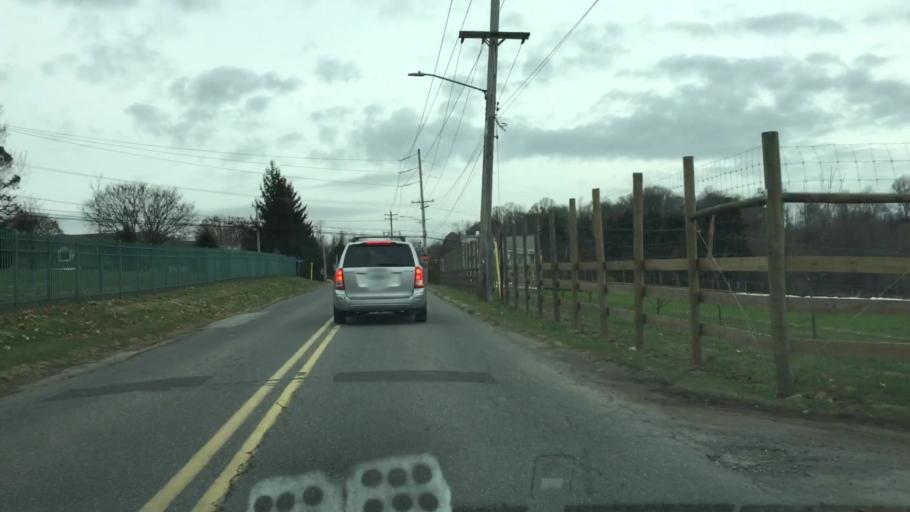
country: US
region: Pennsylvania
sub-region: Delaware County
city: Village Green-Green Ridge
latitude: 39.8737
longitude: -75.4349
